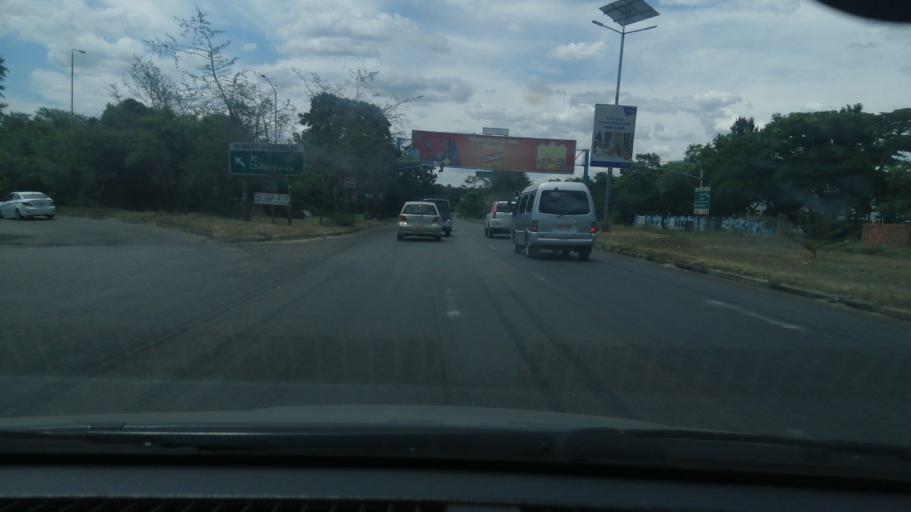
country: ZW
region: Harare
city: Harare
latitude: -17.8344
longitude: 31.1030
